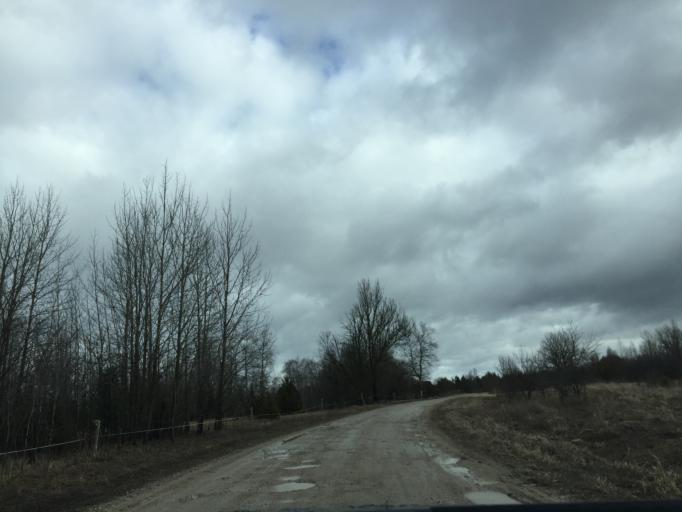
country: EE
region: Laeaene
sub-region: Haapsalu linn
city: Haapsalu
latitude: 58.6841
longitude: 23.5422
